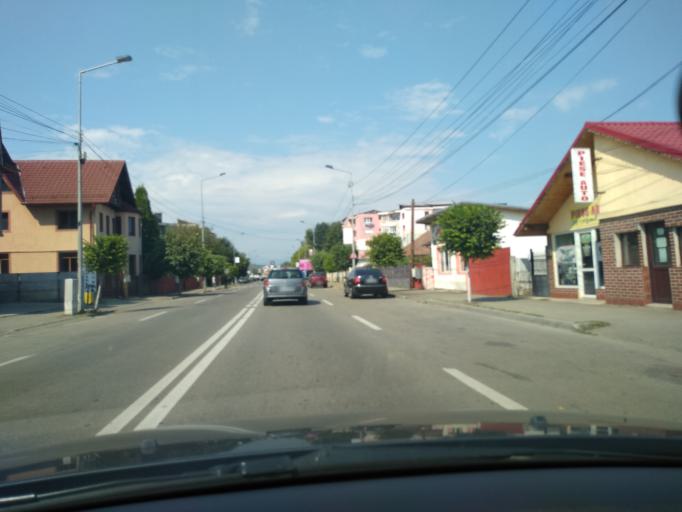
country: RO
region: Gorj
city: Targu Jiu
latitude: 45.0220
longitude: 23.2685
